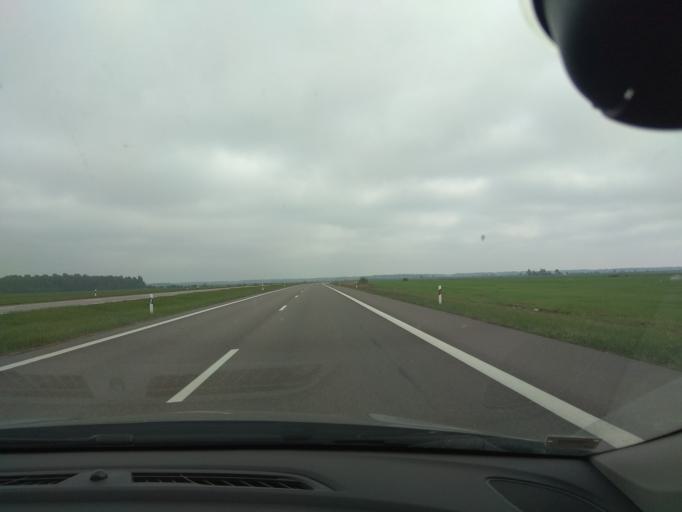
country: LT
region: Panevezys
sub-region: Panevezys City
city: Panevezys
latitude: 55.6092
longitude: 24.4281
